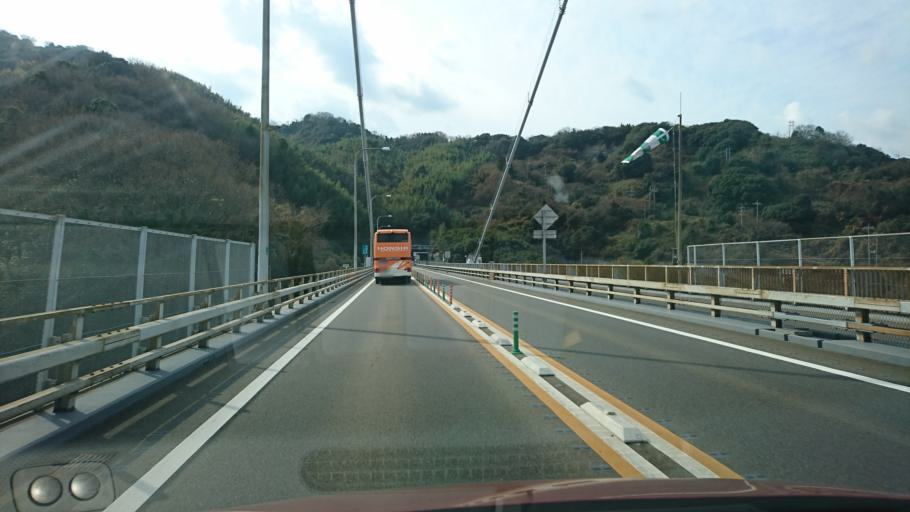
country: JP
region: Hiroshima
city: Innoshima
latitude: 34.1902
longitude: 133.0707
